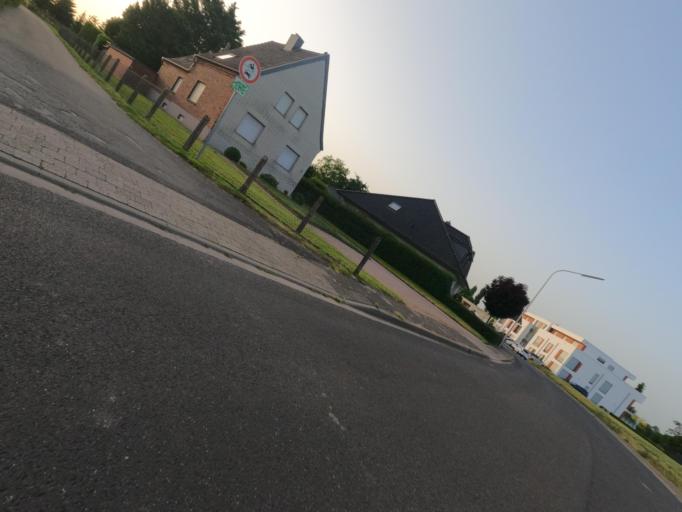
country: DE
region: North Rhine-Westphalia
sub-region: Regierungsbezirk Koln
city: Heinsberg
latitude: 51.0696
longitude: 6.1267
